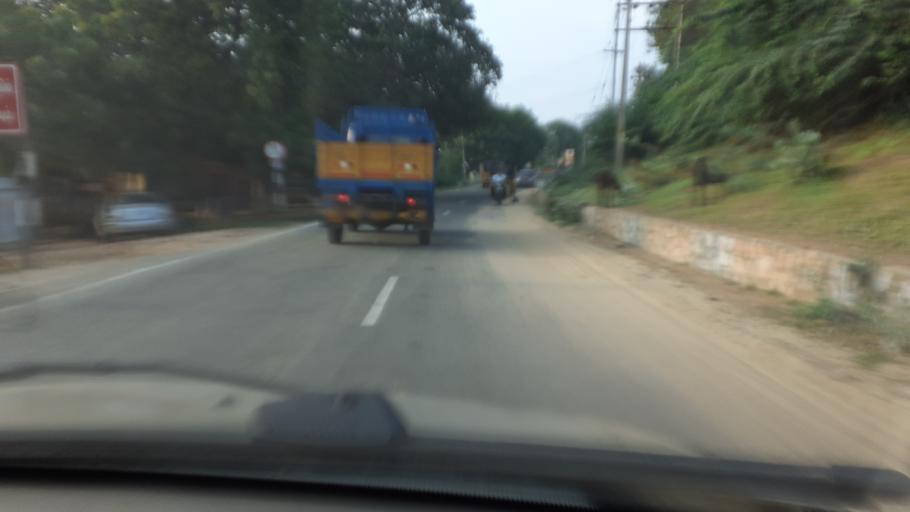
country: IN
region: Tamil Nadu
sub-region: Thoothukkudi
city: Srivaikuntam
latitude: 8.6210
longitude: 77.9108
